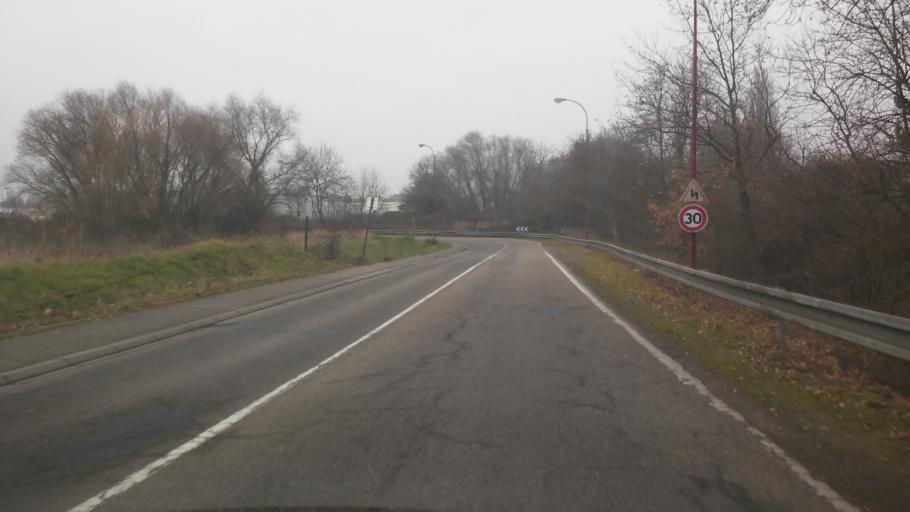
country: FR
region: Lorraine
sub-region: Departement de la Moselle
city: Marly
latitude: 49.0799
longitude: 6.1499
